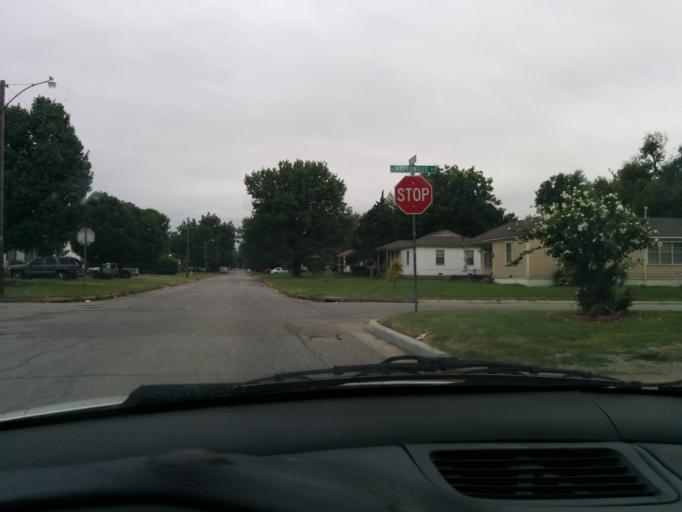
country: US
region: Oklahoma
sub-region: Tulsa County
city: Tulsa
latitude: 36.1680
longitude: -95.9082
